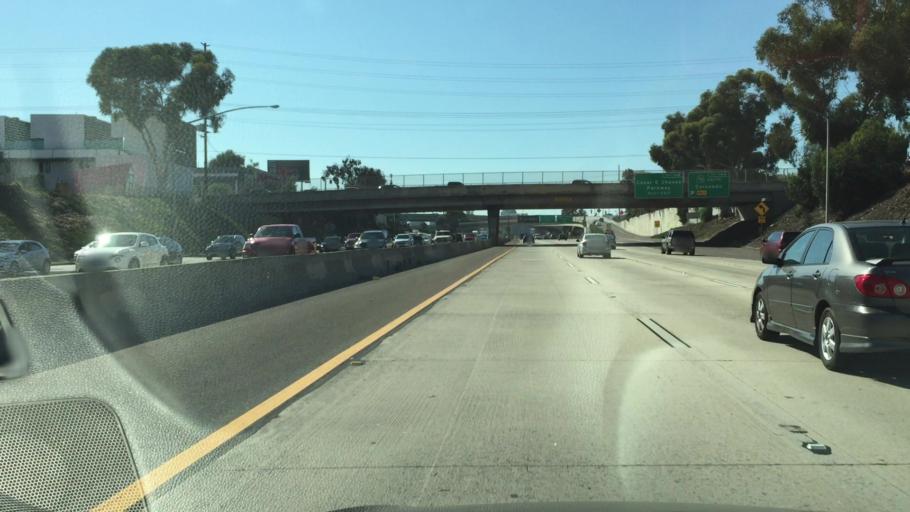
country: US
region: California
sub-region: San Diego County
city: San Diego
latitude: 32.6979
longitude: -117.1379
